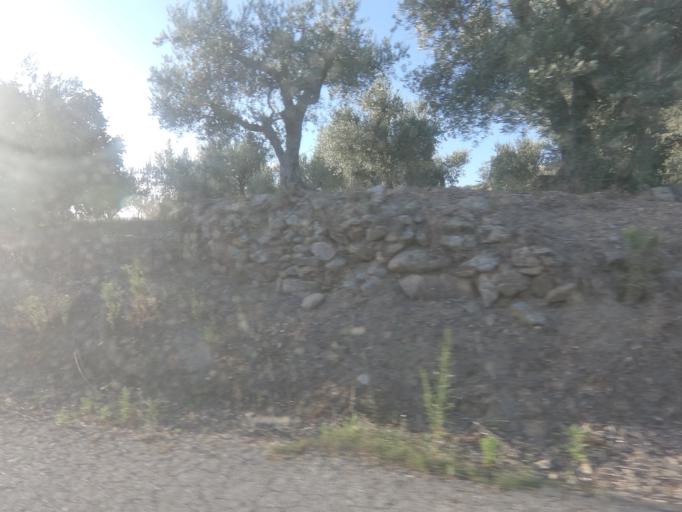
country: PT
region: Viseu
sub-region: Armamar
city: Armamar
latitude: 41.1208
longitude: -7.6691
